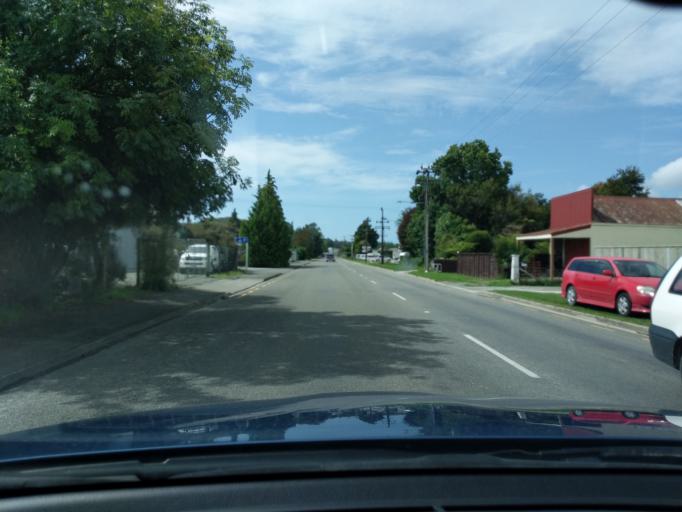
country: NZ
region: Tasman
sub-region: Tasman District
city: Takaka
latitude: -40.8596
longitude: 172.8079
